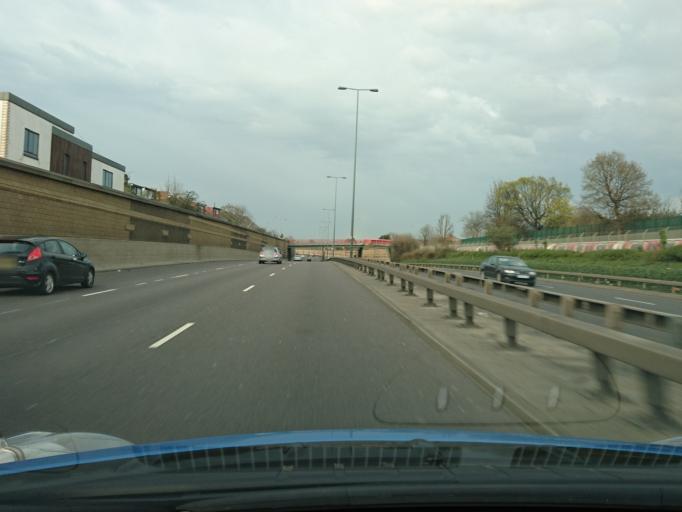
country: GB
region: England
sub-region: Greater London
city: Walthamstow
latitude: 51.5592
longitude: -0.0020
